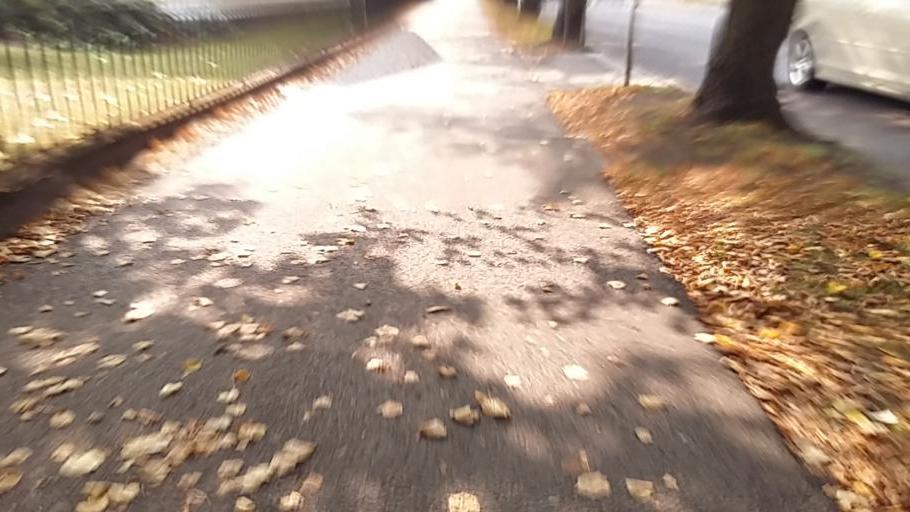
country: SE
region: Joenkoeping
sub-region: Jonkopings Kommun
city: Jonkoping
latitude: 57.7756
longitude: 14.1586
